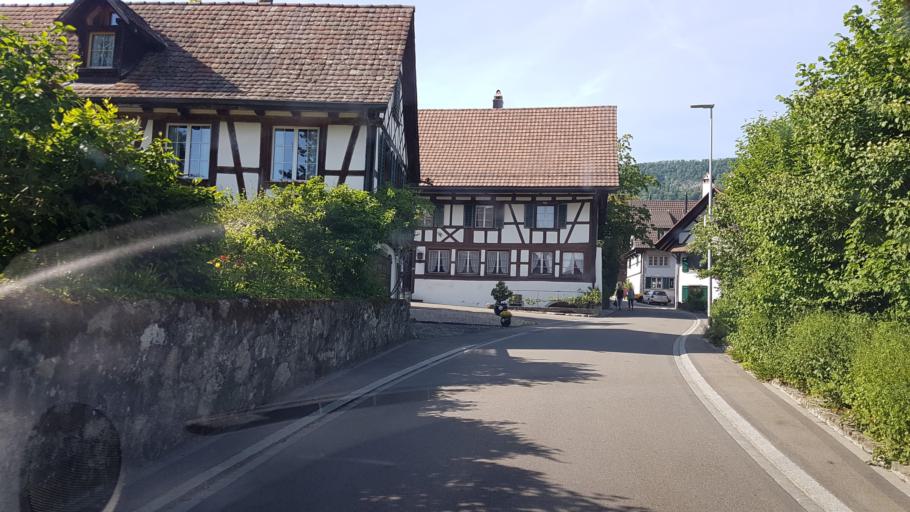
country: CH
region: Zurich
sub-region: Bezirk Dielsdorf
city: Otelfingen
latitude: 47.4640
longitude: 8.3871
